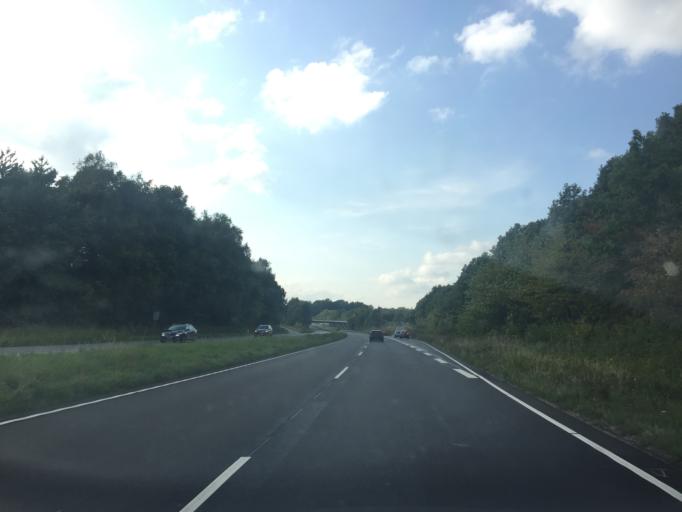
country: DK
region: Zealand
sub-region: Holbaek Kommune
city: Jyderup
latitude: 55.6619
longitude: 11.4141
